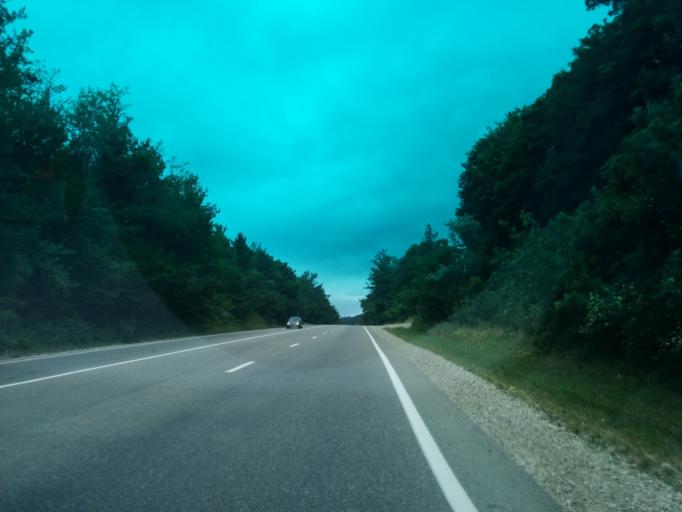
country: RU
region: Krasnodarskiy
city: Ol'ginka
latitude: 44.1794
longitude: 38.9387
